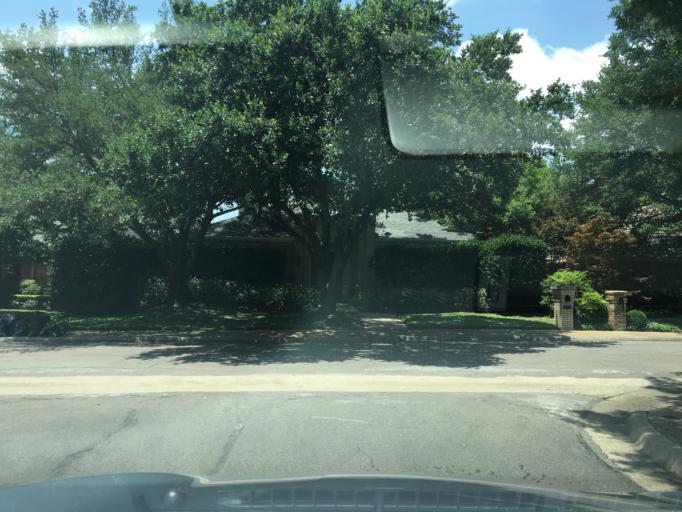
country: US
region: Texas
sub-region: Dallas County
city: Addison
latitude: 32.9191
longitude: -96.8063
